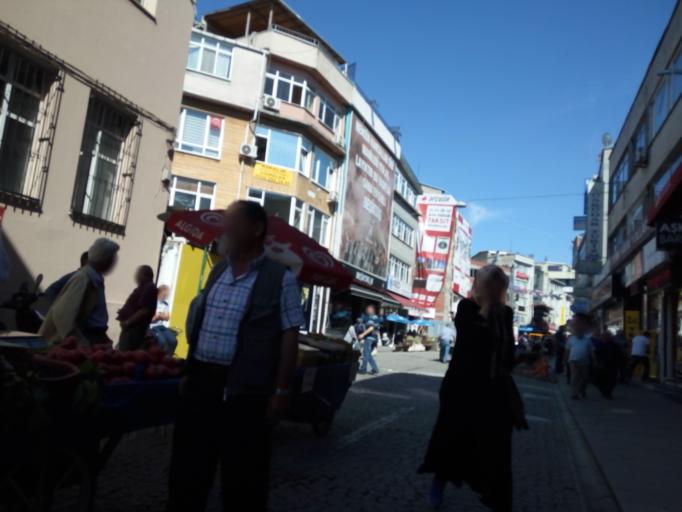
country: TR
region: Istanbul
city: UEskuedar
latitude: 41.0247
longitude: 29.0171
